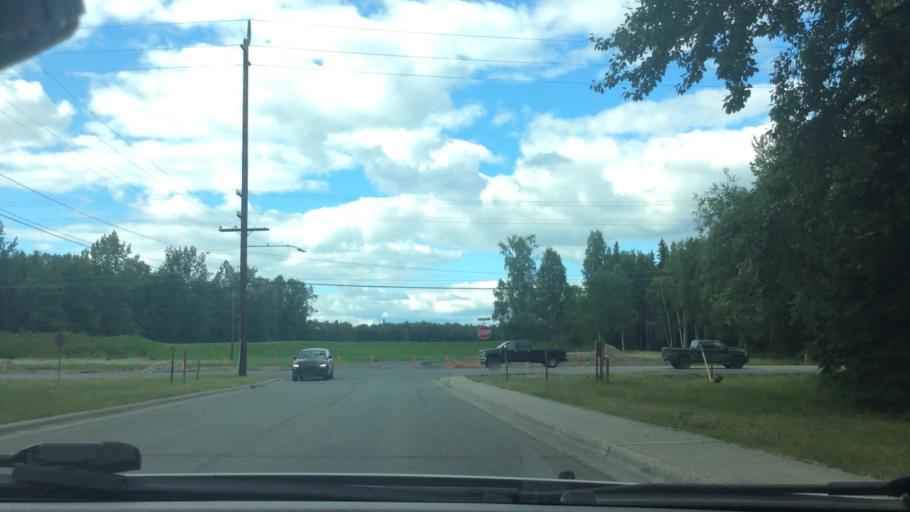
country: US
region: Alaska
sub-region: Anchorage Municipality
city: Elmendorf Air Force Base
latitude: 61.2308
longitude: -149.7554
